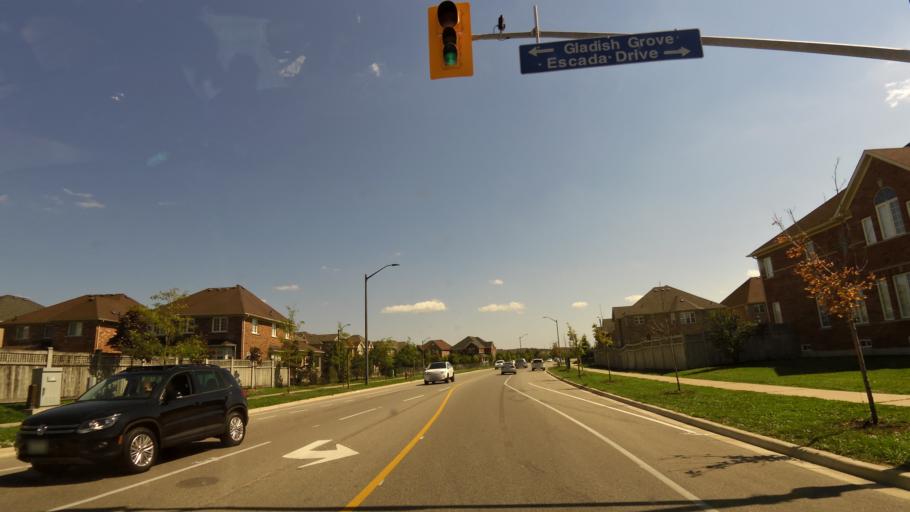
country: CA
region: Ontario
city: Mississauga
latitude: 43.5501
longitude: -79.7298
